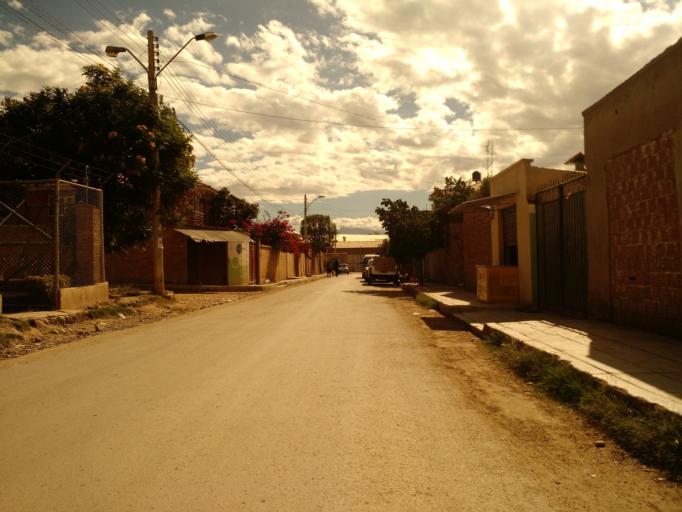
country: BO
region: Cochabamba
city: Cochabamba
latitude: -17.4579
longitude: -66.1551
